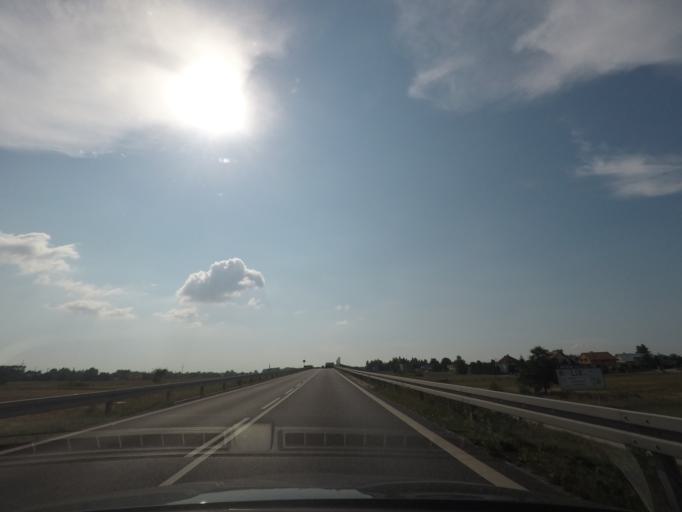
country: PL
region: Silesian Voivodeship
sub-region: Powiat pszczynski
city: Czarkow
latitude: 50.0013
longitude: 18.9230
